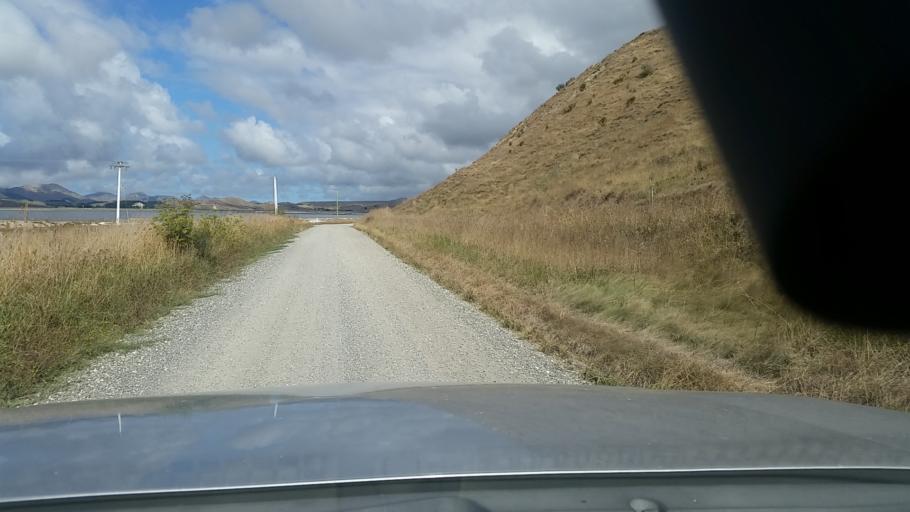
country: NZ
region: Marlborough
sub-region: Marlborough District
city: Blenheim
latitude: -41.7038
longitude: 174.1499
